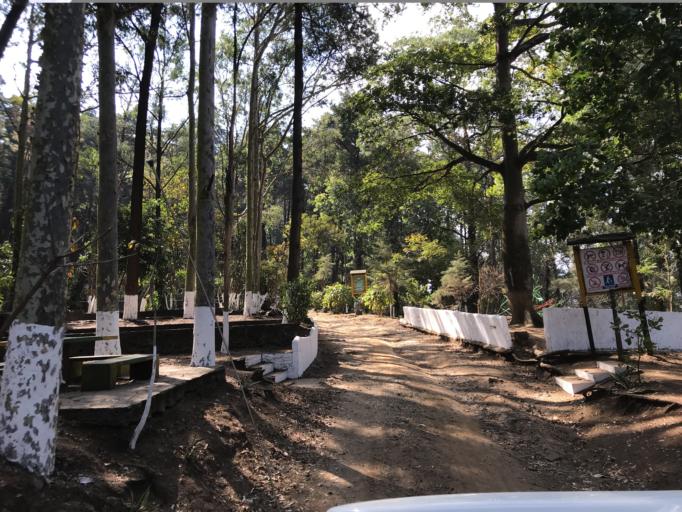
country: GT
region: Guatemala
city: Petapa
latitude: 14.4840
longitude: -90.5570
